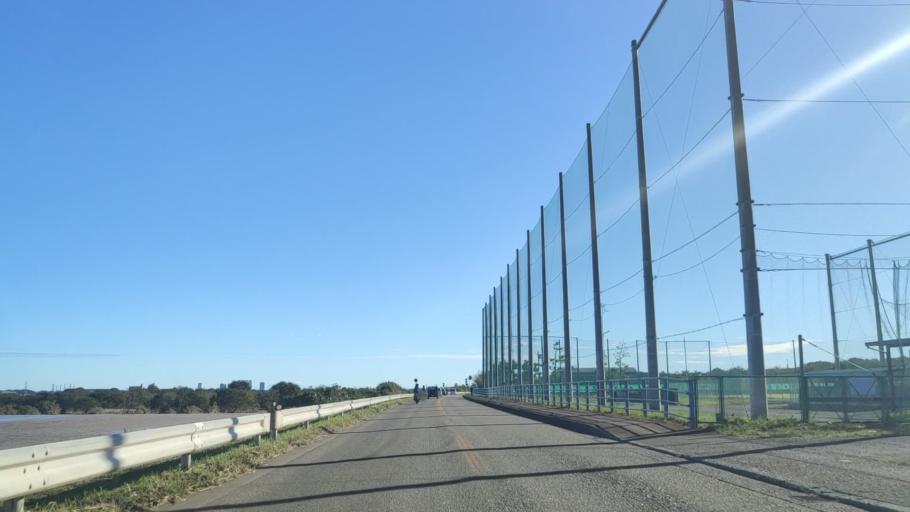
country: JP
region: Kanagawa
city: Zama
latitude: 35.5106
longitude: 139.3742
